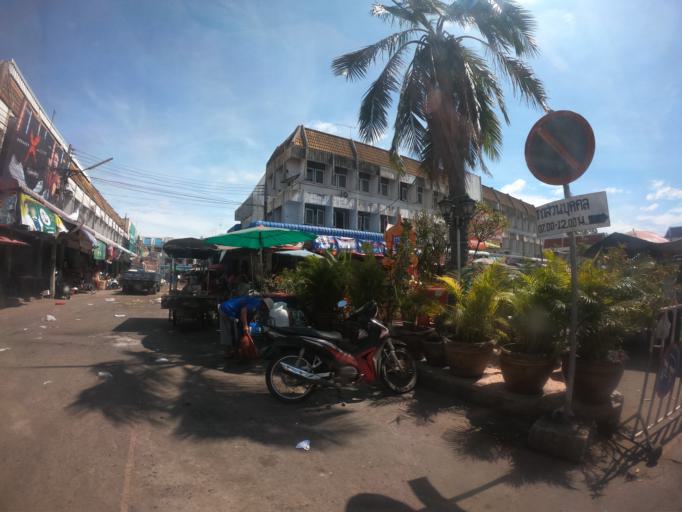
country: TH
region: Surin
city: Prasat
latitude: 14.6368
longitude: 103.4075
